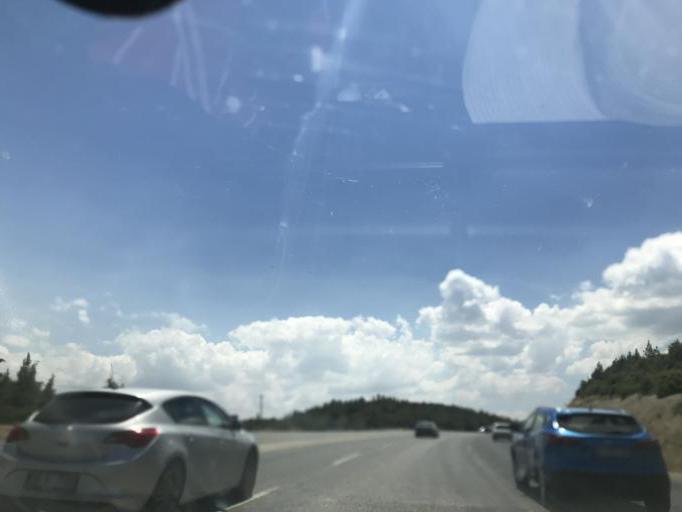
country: TR
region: Denizli
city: Honaz
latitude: 37.7062
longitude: 29.2045
